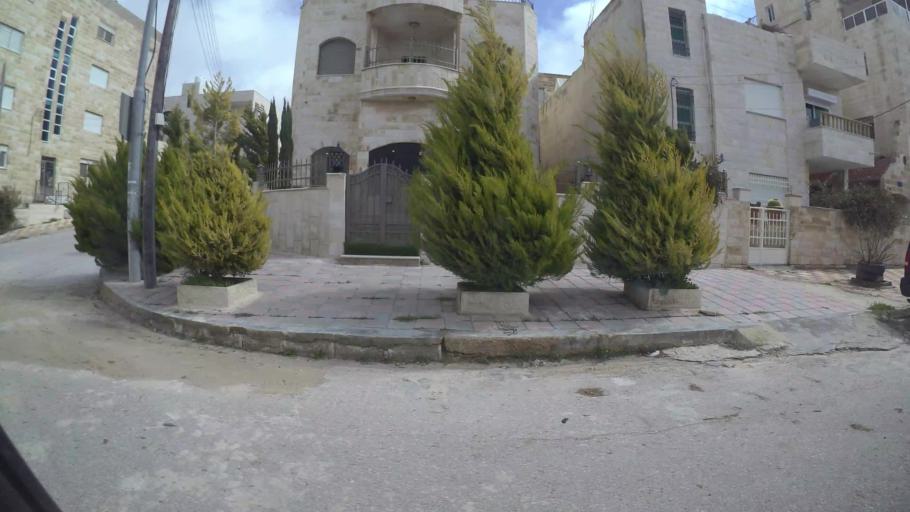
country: JO
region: Amman
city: Al Jubayhah
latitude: 32.0677
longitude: 35.8785
